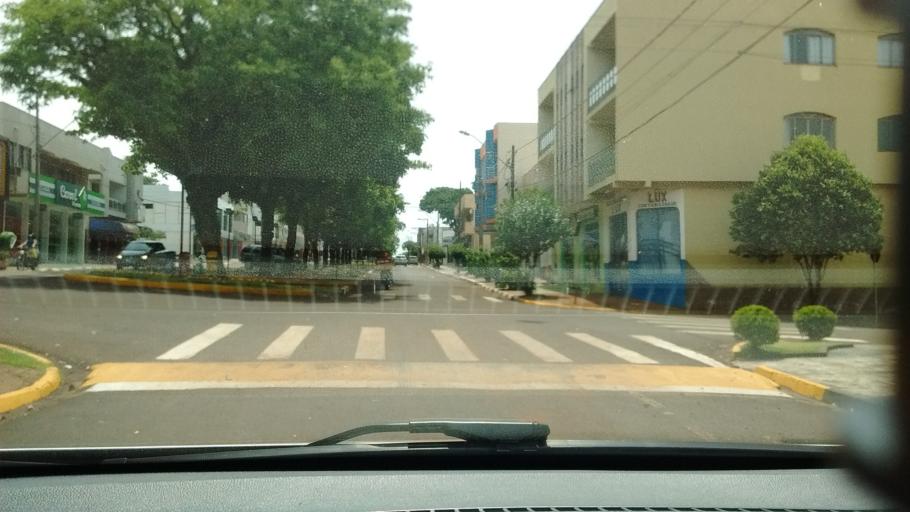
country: BR
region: Parana
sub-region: Corbelia
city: Corbelia
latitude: -24.5424
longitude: -52.9876
